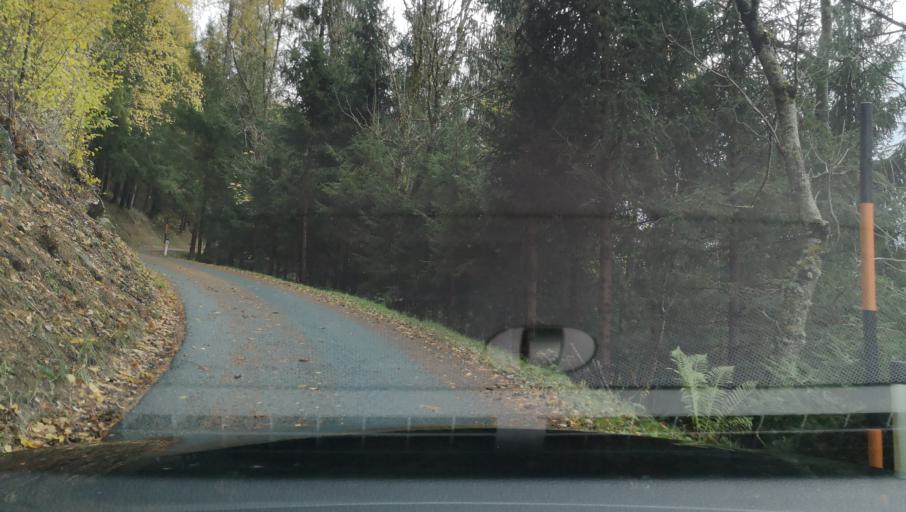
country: AT
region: Styria
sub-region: Politischer Bezirk Weiz
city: Birkfeld
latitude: 47.3689
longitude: 15.6316
